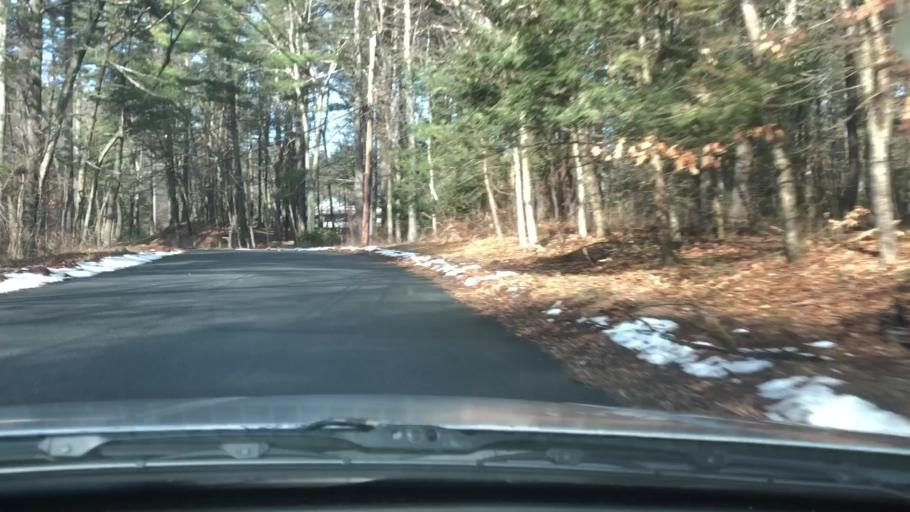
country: US
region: Massachusetts
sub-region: Middlesex County
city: West Concord
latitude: 42.5003
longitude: -71.3934
